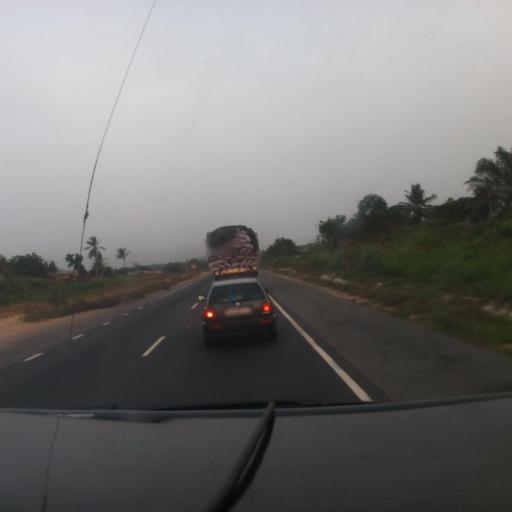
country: GH
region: Eastern
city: Nsawam
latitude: 5.8964
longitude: -0.3861
